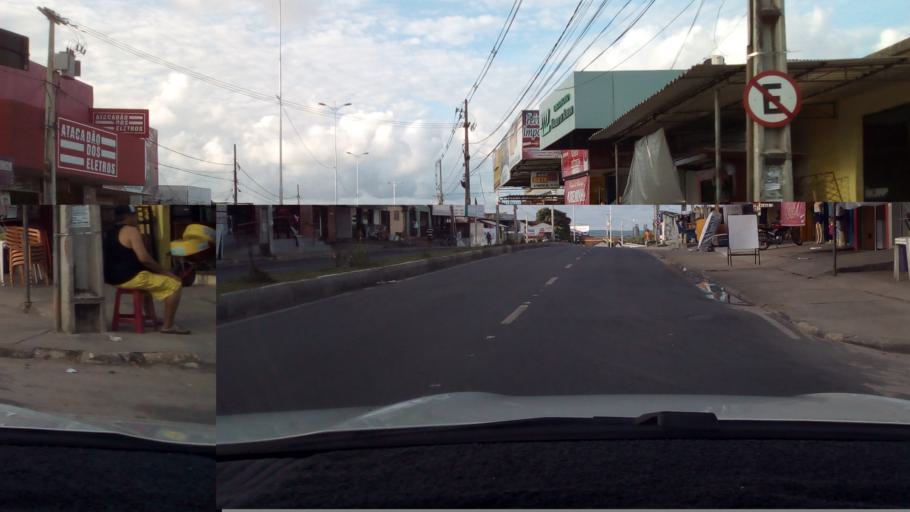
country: BR
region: Paraiba
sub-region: Bayeux
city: Bayeux
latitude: -7.1576
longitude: -34.8961
